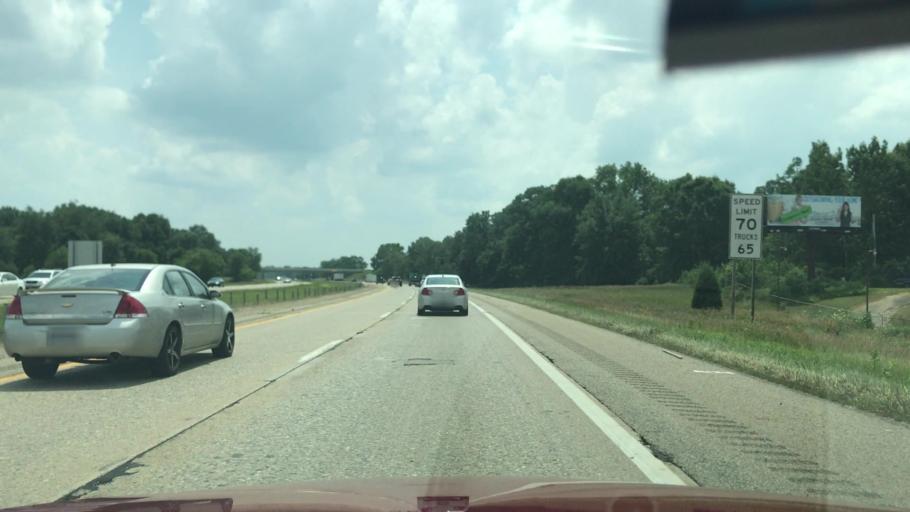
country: US
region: Michigan
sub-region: Allegan County
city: Plainwell
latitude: 42.4399
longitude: -85.6606
